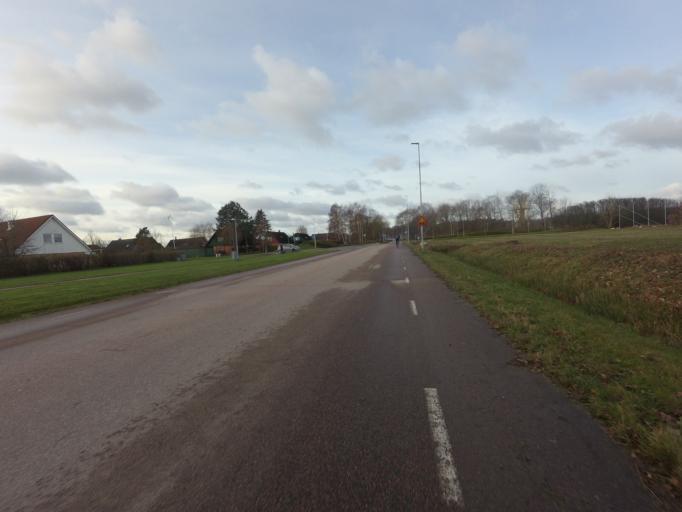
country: SE
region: Skane
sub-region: Hoganas Kommun
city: Hoganas
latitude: 56.1817
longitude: 12.5690
